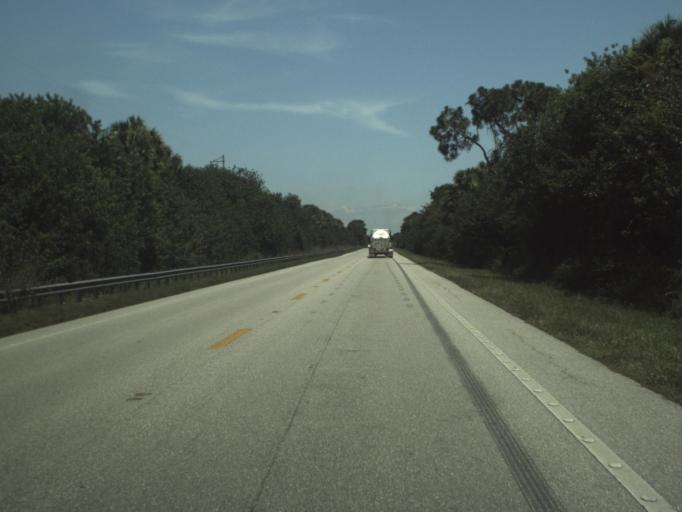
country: US
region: Florida
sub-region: Martin County
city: Indiantown
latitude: 27.1124
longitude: -80.6070
